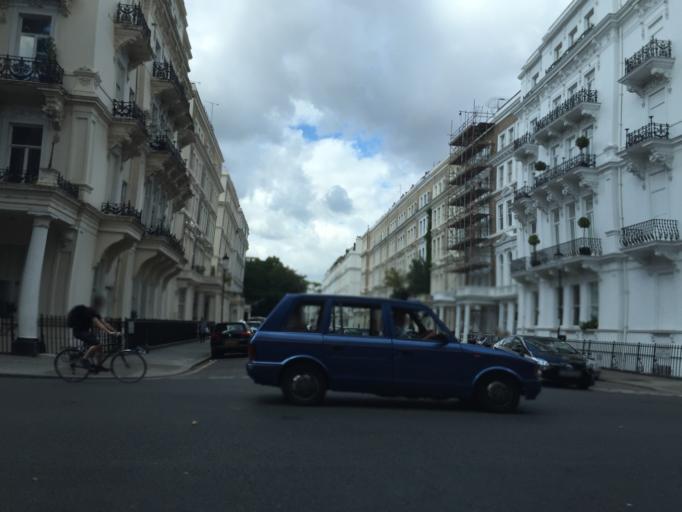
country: GB
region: England
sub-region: Greater London
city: Kensington
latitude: 51.4970
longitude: -0.1795
